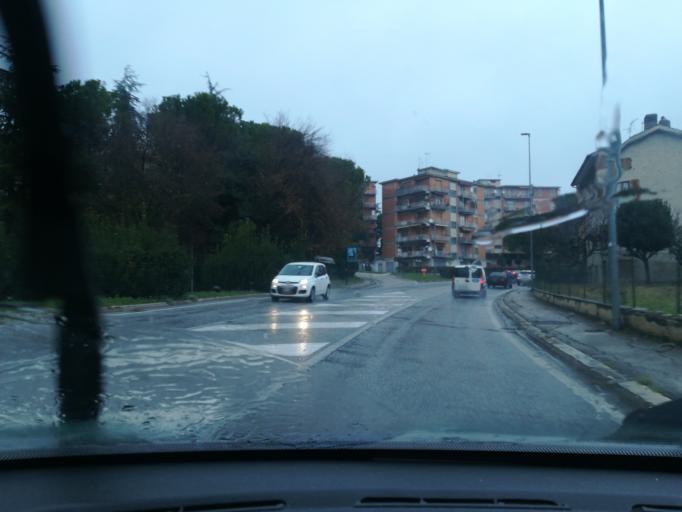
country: IT
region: The Marches
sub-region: Provincia di Macerata
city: Macerata
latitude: 43.2857
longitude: 13.4325
